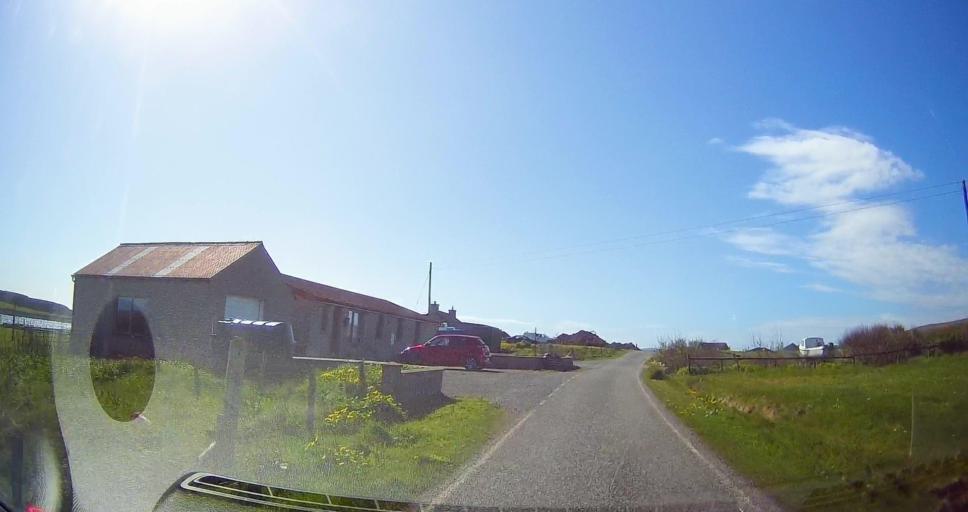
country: GB
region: Scotland
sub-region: Shetland Islands
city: Sandwick
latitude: 60.0389
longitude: -1.2181
